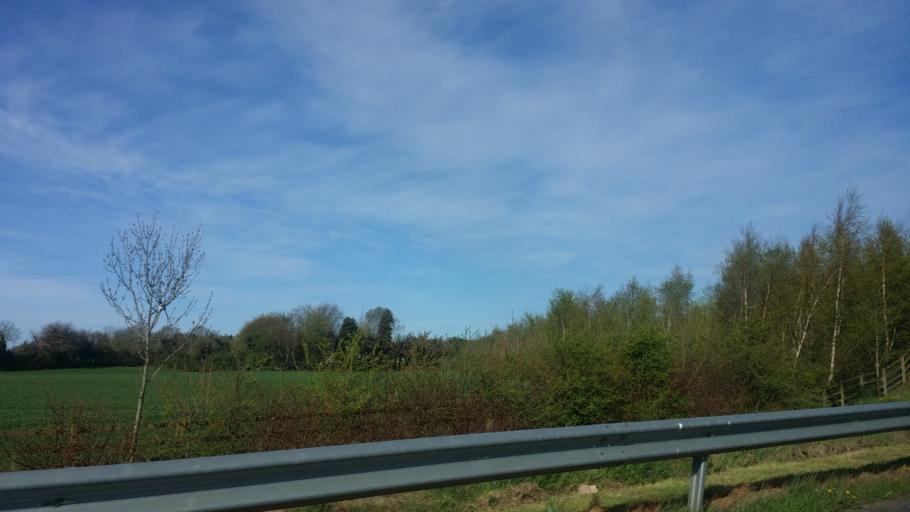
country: IE
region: Leinster
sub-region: An Mhi
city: Kells
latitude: 53.6786
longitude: -6.7949
